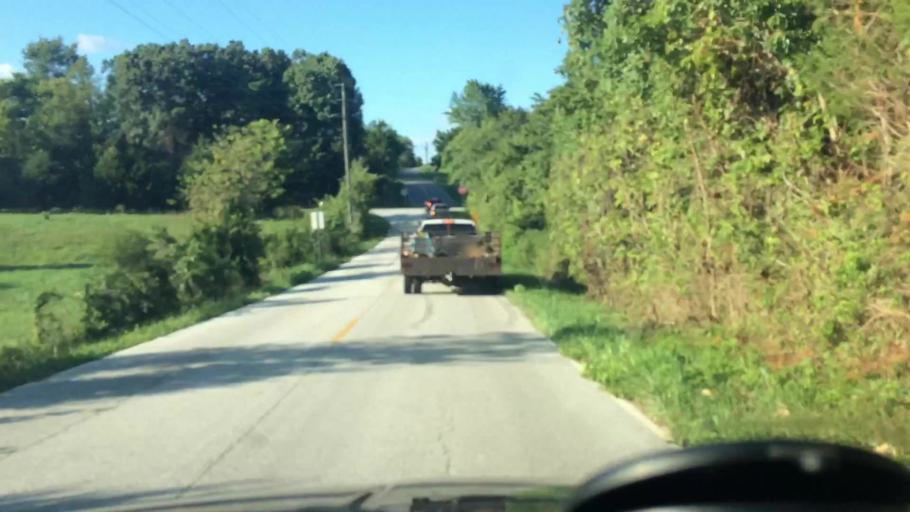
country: US
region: Missouri
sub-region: Greene County
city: Strafford
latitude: 37.2848
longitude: -93.0938
